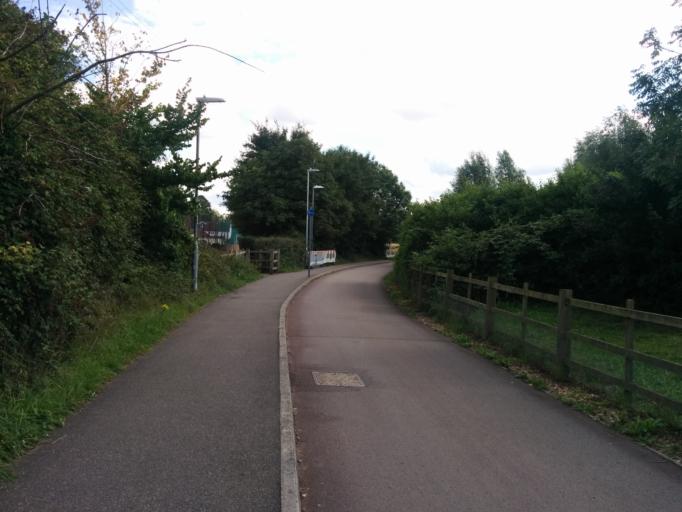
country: GB
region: England
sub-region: Cambridgeshire
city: Cambridge
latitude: 52.2078
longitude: 0.0963
